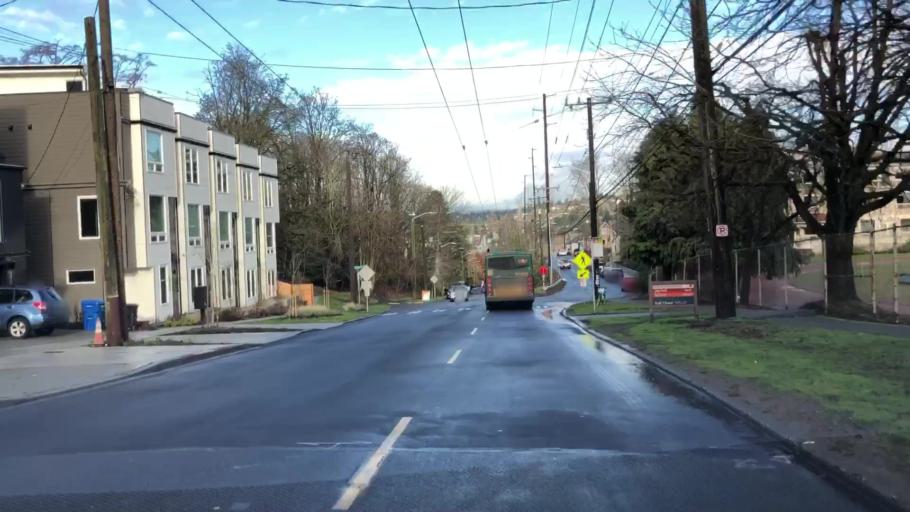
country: US
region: Washington
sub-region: King County
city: Seattle
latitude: 47.6451
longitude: -122.3608
